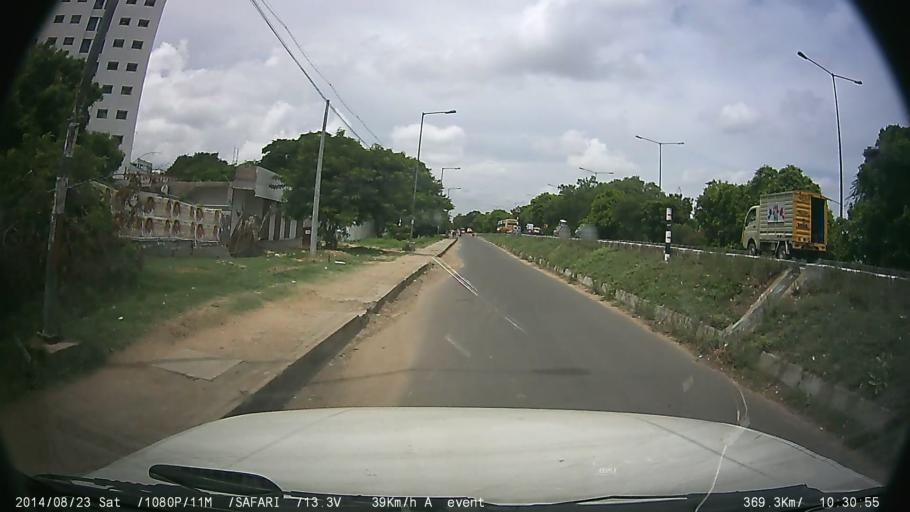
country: IN
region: Tamil Nadu
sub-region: Kancheepuram
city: Guduvancheri
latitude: 12.8275
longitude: 80.0426
